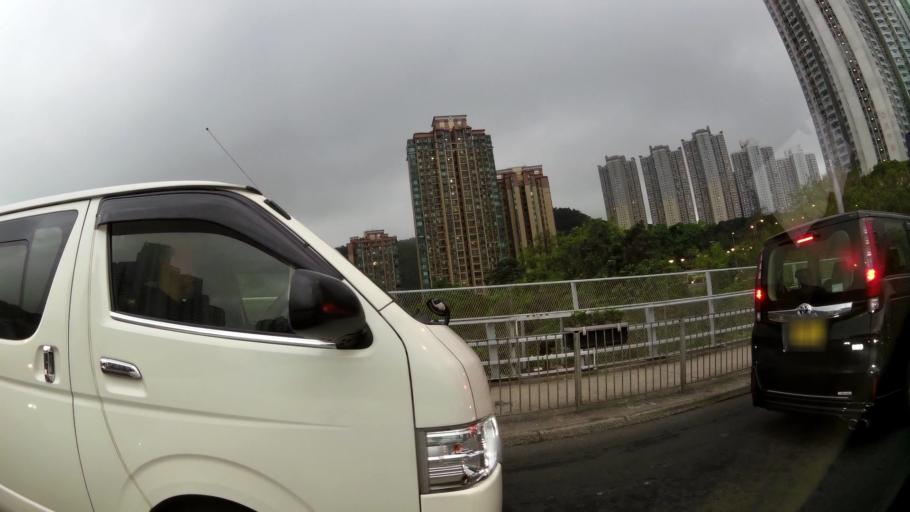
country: HK
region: Tsuen Wan
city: Tsuen Wan
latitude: 22.3520
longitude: 114.0982
